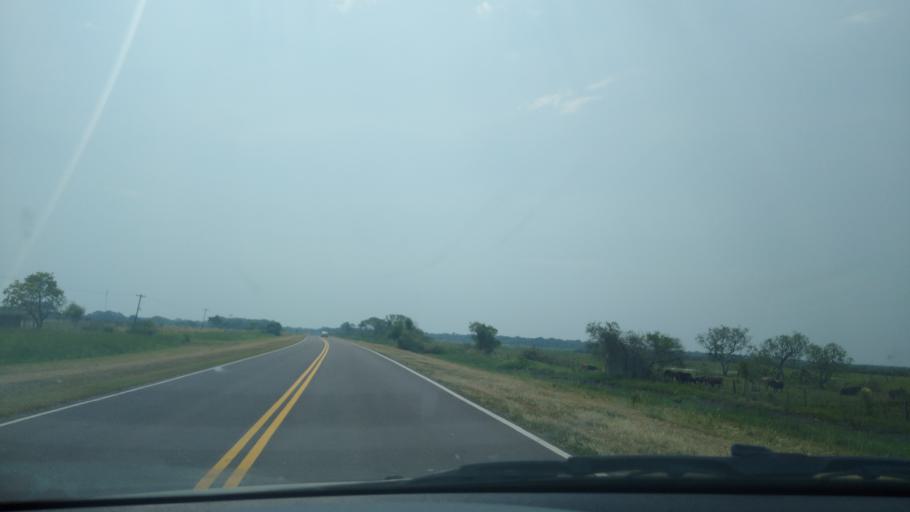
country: AR
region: Chaco
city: La Eduvigis
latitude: -26.8507
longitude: -59.0474
